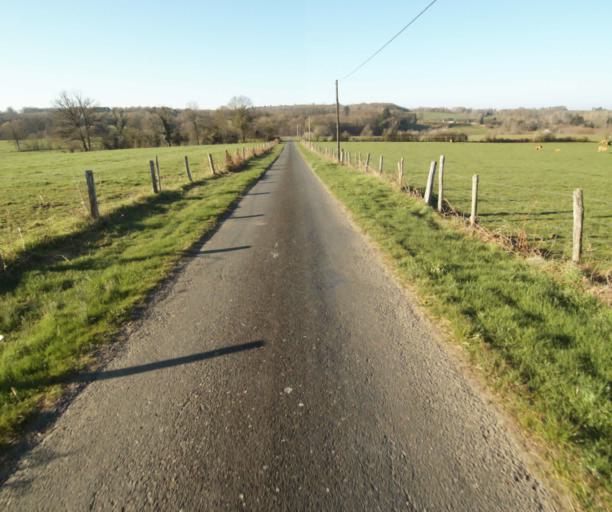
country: FR
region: Limousin
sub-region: Departement de la Correze
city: Uzerche
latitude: 45.3815
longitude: 1.5856
